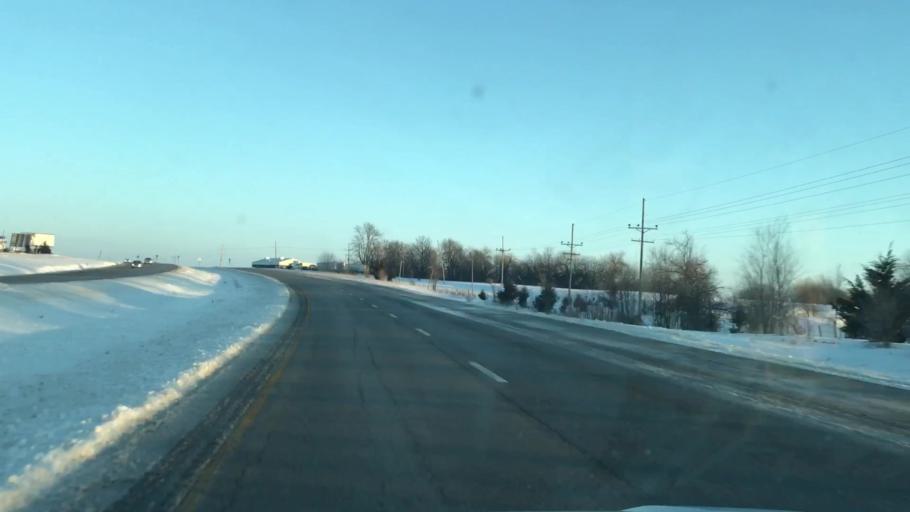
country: US
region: Missouri
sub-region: Clinton County
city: Cameron
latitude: 39.7558
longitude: -94.3416
